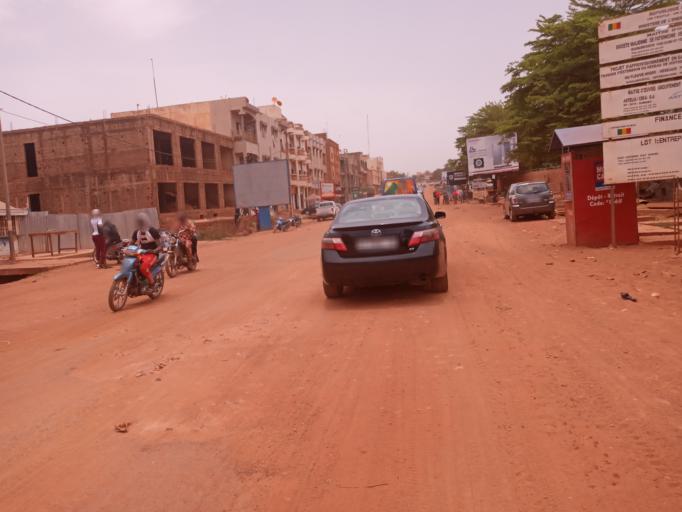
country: ML
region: Bamako
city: Bamako
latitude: 12.5758
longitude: -8.0104
